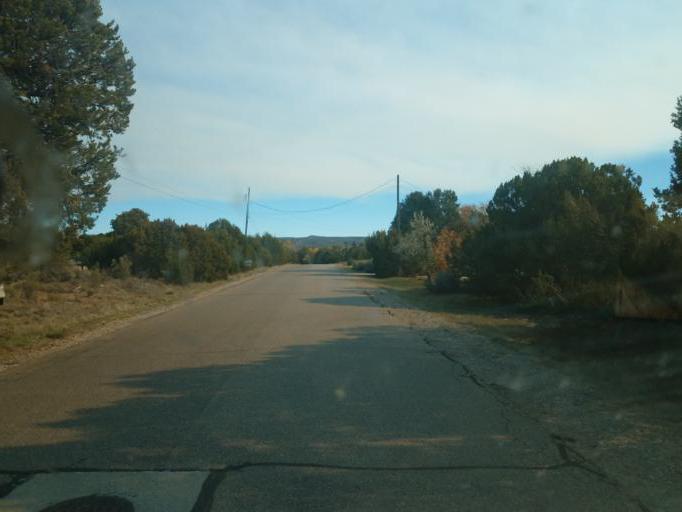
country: US
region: New Mexico
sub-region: Los Alamos County
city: White Rock
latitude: 35.8121
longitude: -106.2212
